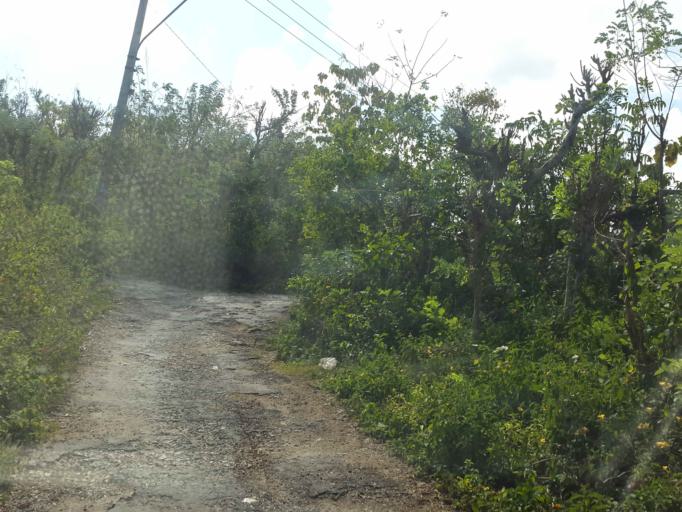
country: ID
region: Bali
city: Pondokkaha Kelod
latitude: -8.7507
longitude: 115.4908
